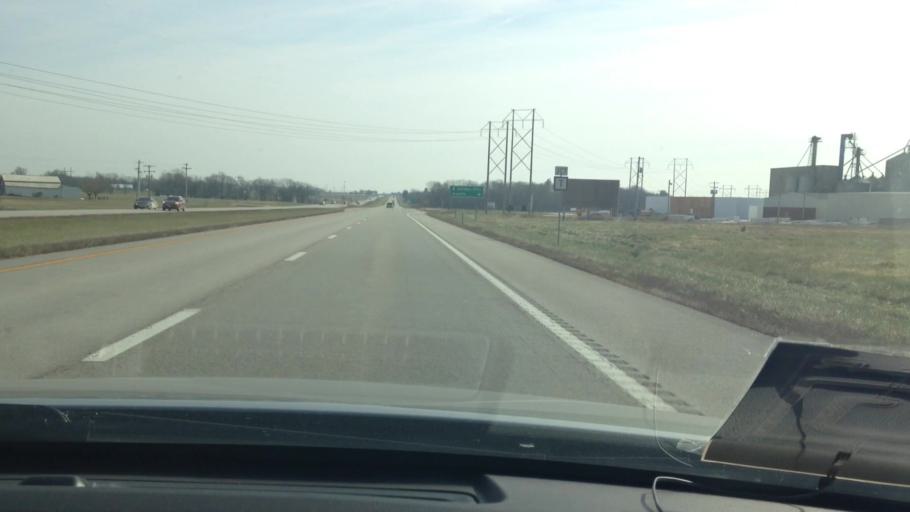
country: US
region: Missouri
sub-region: Cass County
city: Garden City
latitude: 38.5960
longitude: -94.2507
